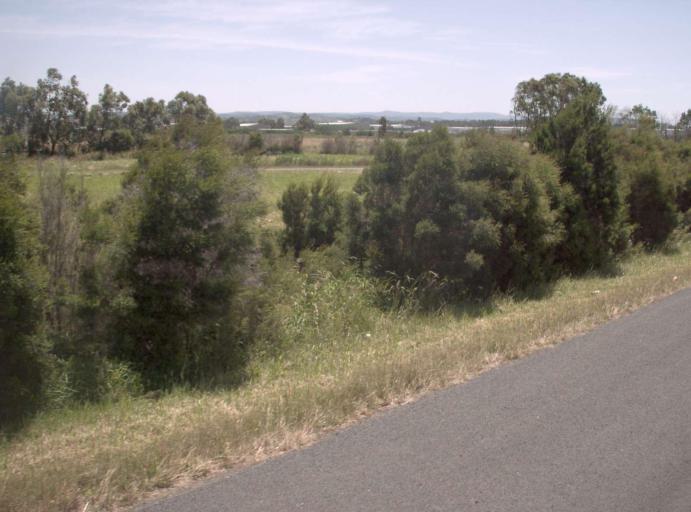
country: AU
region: Victoria
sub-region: Cardinia
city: Pakenham South
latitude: -38.0915
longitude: 145.4931
